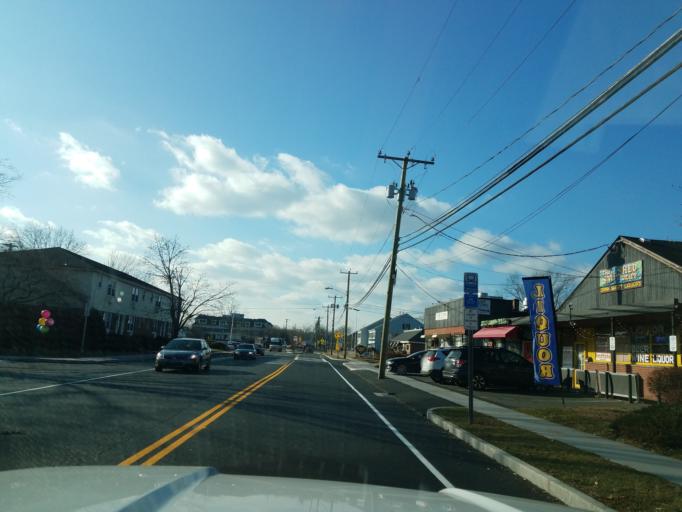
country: US
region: Connecticut
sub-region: Hartford County
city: Glastonbury
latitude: 41.7132
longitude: -72.6031
